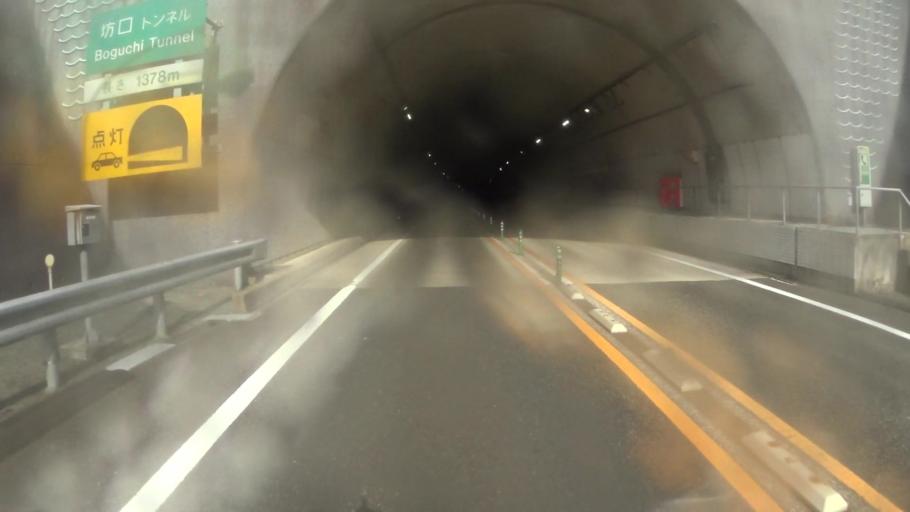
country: JP
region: Kyoto
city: Ayabe
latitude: 35.3950
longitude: 135.2360
